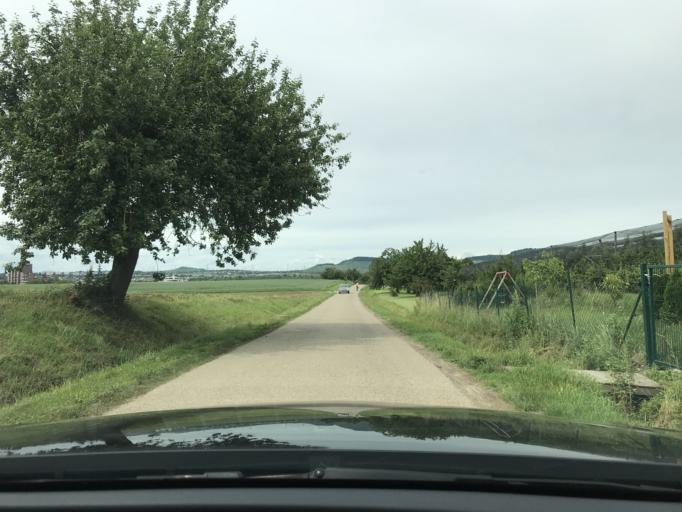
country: DE
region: Baden-Wuerttemberg
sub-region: Regierungsbezirk Stuttgart
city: Weinstadt-Endersbach
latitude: 48.8012
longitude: 9.3604
